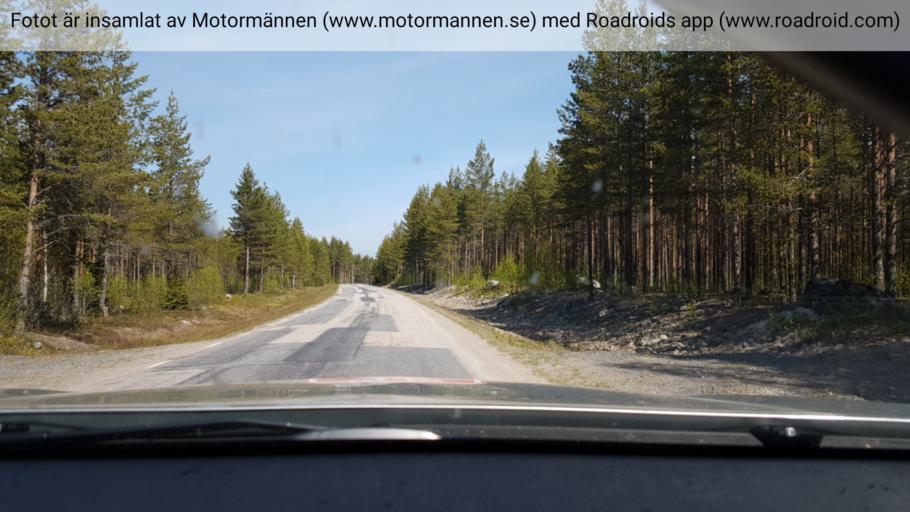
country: SE
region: Vaesterbotten
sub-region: Umea Kommun
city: Saevar
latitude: 63.8185
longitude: 20.5862
